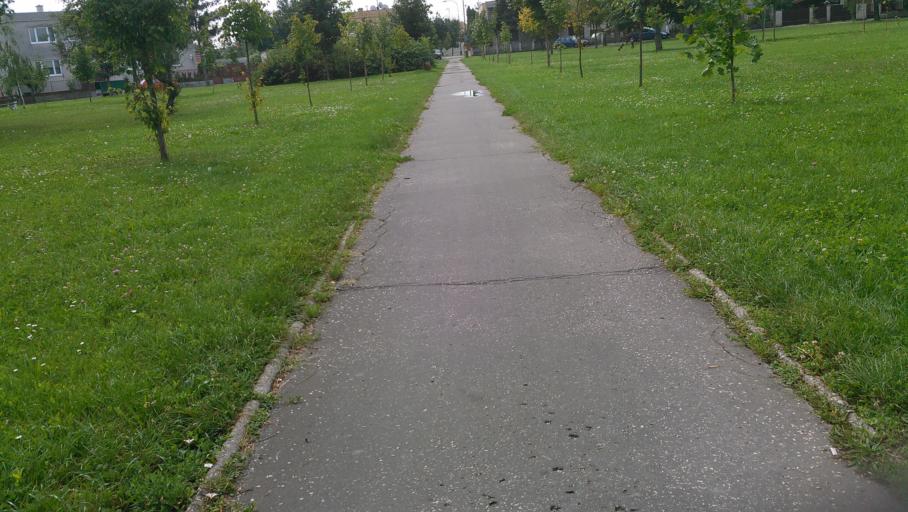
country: SK
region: Nitriansky
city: Kolarovo
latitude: 47.9127
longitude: 17.9921
